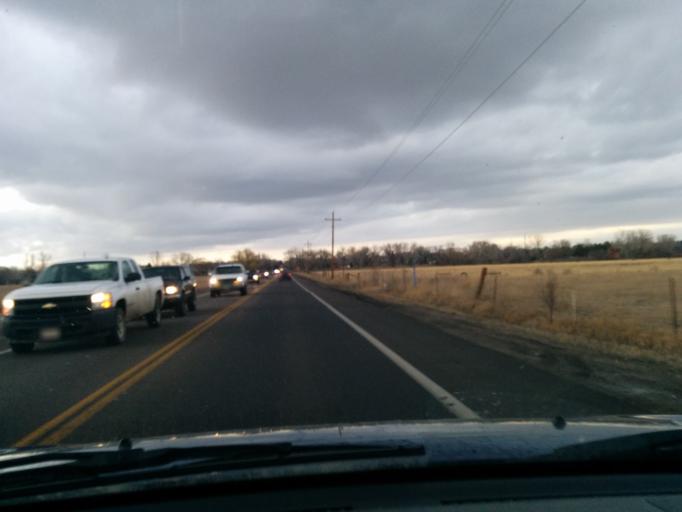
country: US
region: Colorado
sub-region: Larimer County
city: Fort Collins
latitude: 40.5986
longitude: -105.0576
